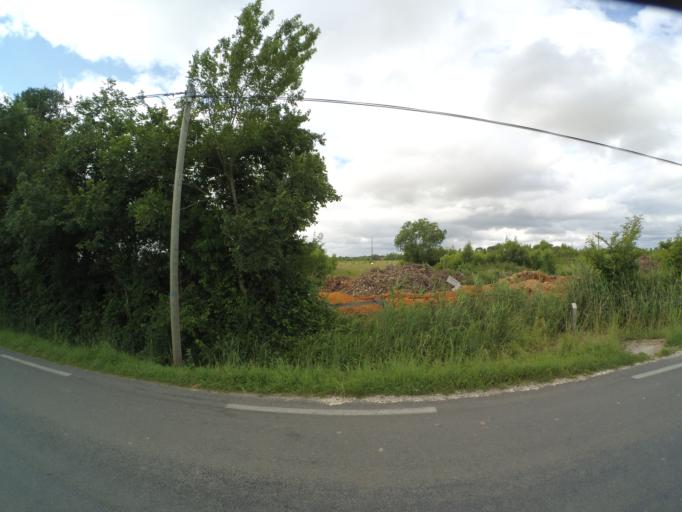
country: FR
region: Aquitaine
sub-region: Departement de la Gironde
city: Ludon-Medoc
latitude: 44.9882
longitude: -0.5771
